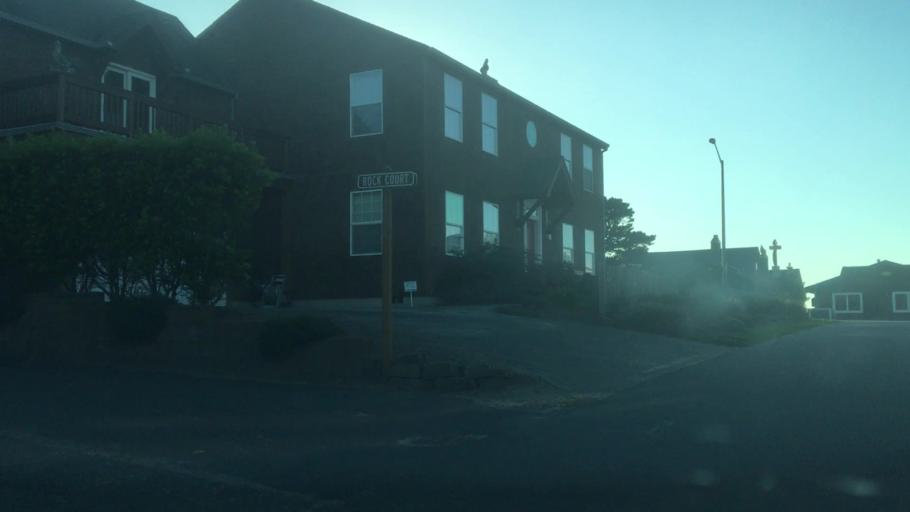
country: US
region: Oregon
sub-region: Clatsop County
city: Cannon Beach
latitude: 45.8888
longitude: -123.9625
